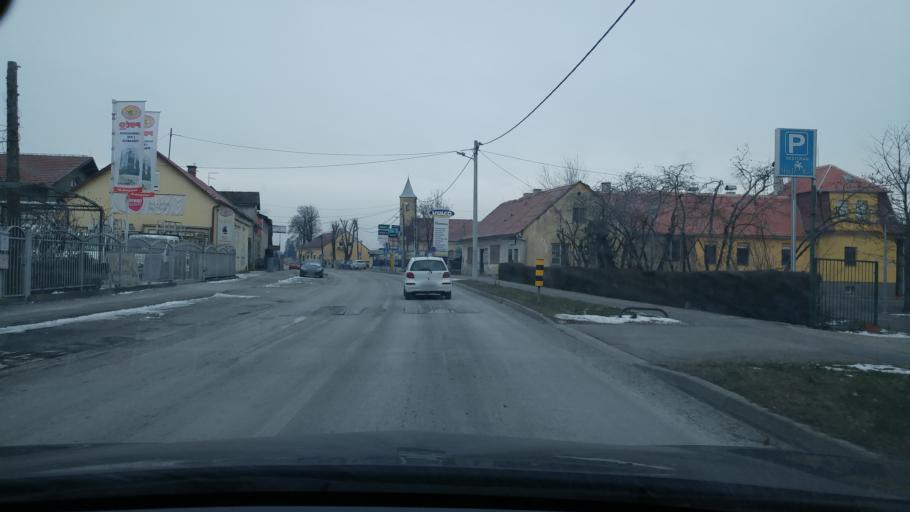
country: HR
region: Grad Zagreb
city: Stenjevec
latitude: 45.8121
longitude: 15.8881
